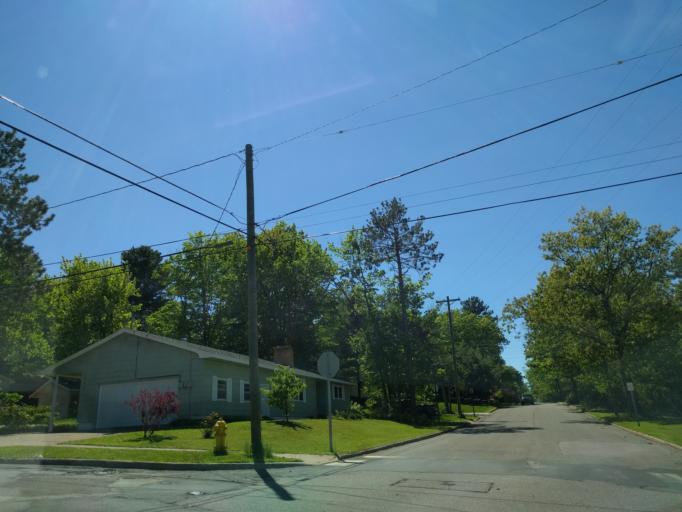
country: US
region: Michigan
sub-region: Marquette County
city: Marquette
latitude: 46.5604
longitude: -87.4120
